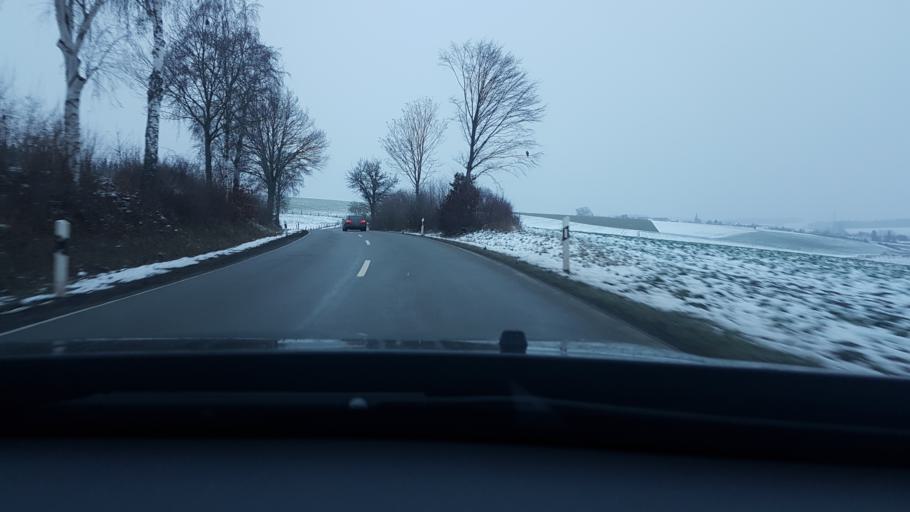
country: DE
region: North Rhine-Westphalia
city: Marsberg
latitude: 51.3808
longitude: 8.8720
